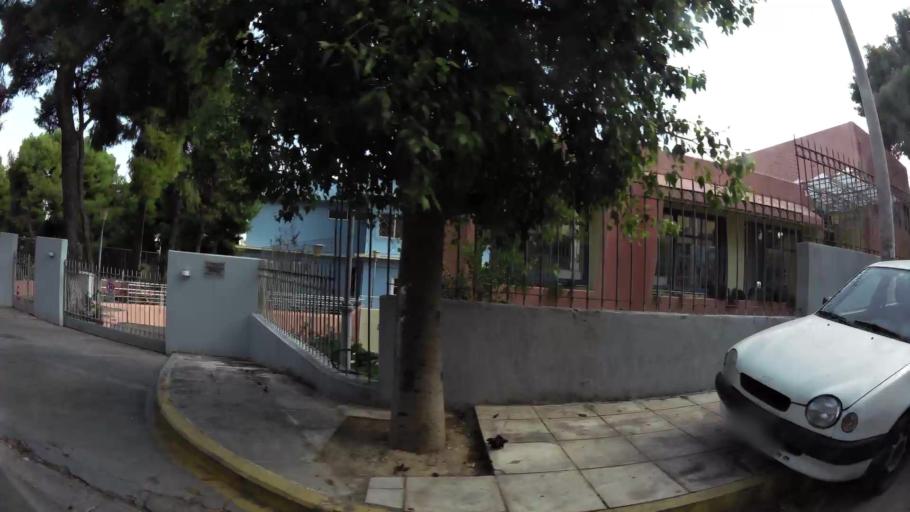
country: GR
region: Attica
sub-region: Nomarchia Athinas
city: Cholargos
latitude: 37.9987
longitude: 23.8028
